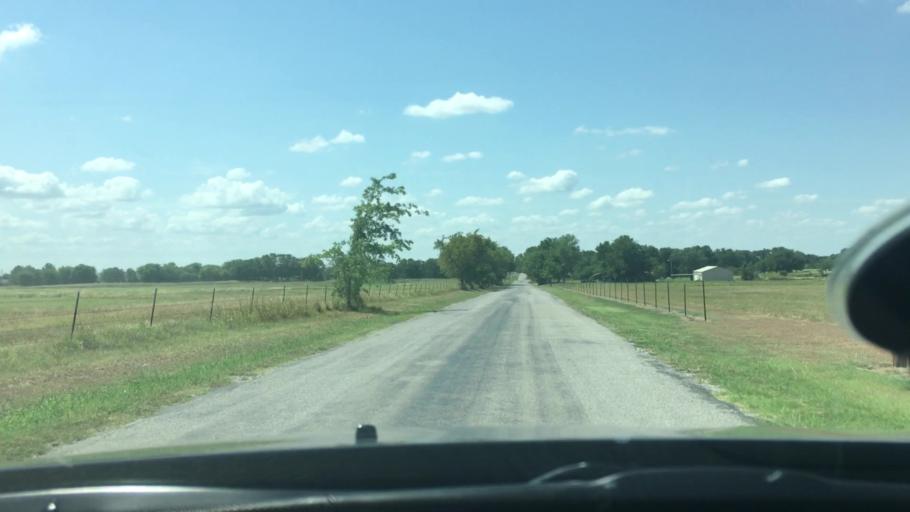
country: US
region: Oklahoma
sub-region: Love County
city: Marietta
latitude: 33.9301
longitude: -97.1608
